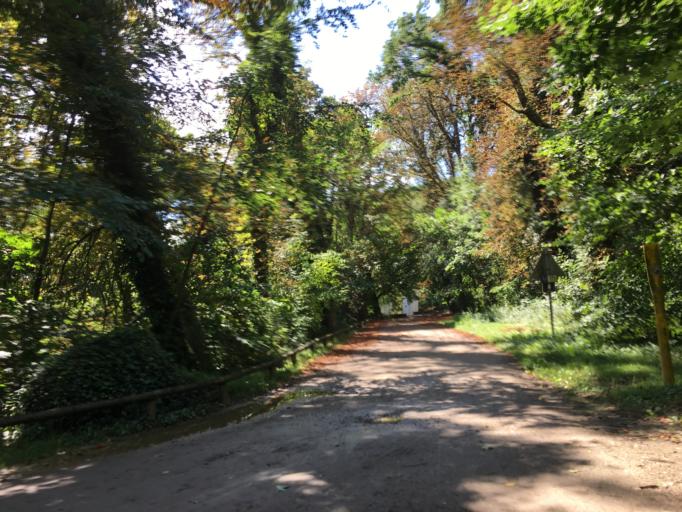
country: DE
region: North Rhine-Westphalia
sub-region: Regierungsbezirk Koln
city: Dueren
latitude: 50.7837
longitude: 6.4932
